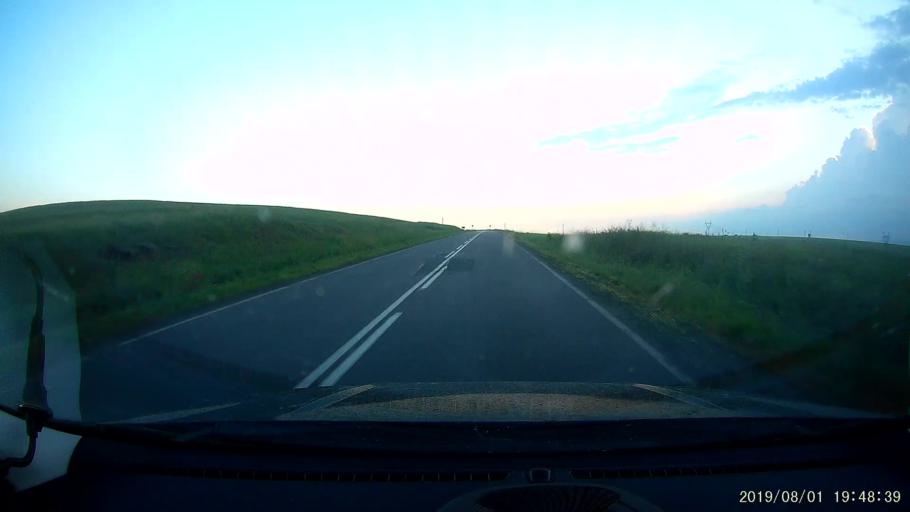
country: BG
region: Burgas
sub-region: Obshtina Karnobat
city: Karnobat
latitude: 42.6335
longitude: 26.9458
